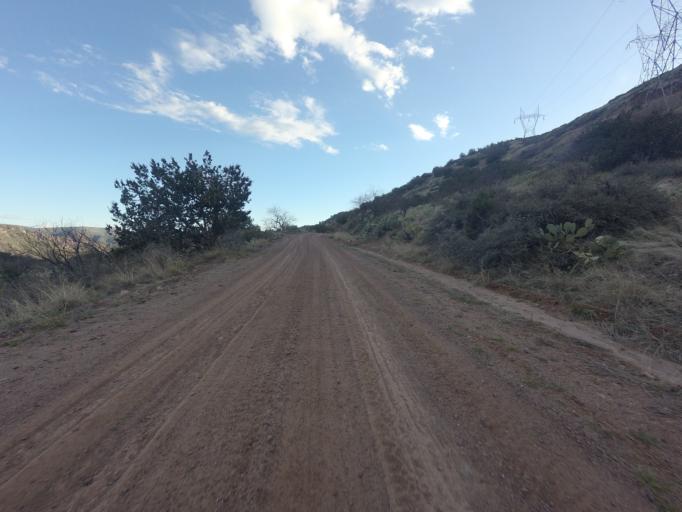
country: US
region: Arizona
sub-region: Gila County
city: Pine
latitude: 34.3638
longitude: -111.6759
